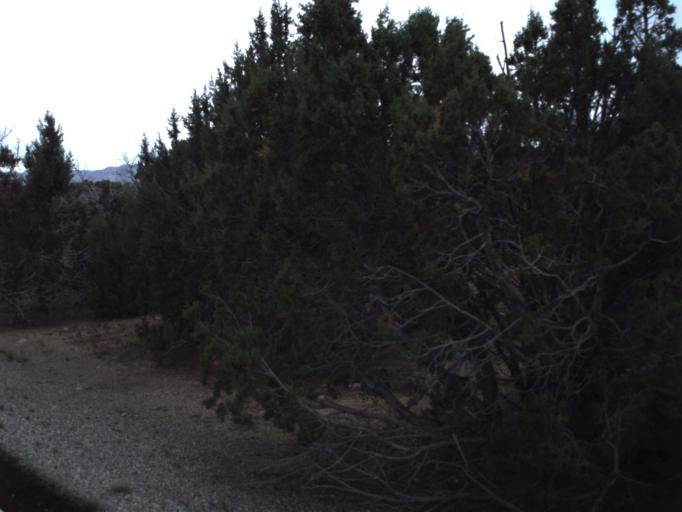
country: US
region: Utah
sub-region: Carbon County
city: East Carbon City
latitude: 39.4617
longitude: -110.3910
